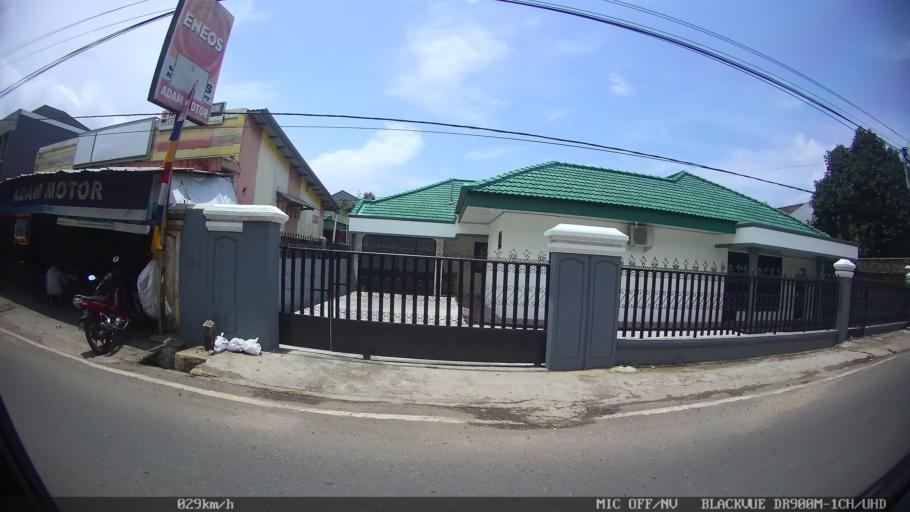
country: ID
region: Lampung
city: Kedaton
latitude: -5.3899
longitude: 105.2493
